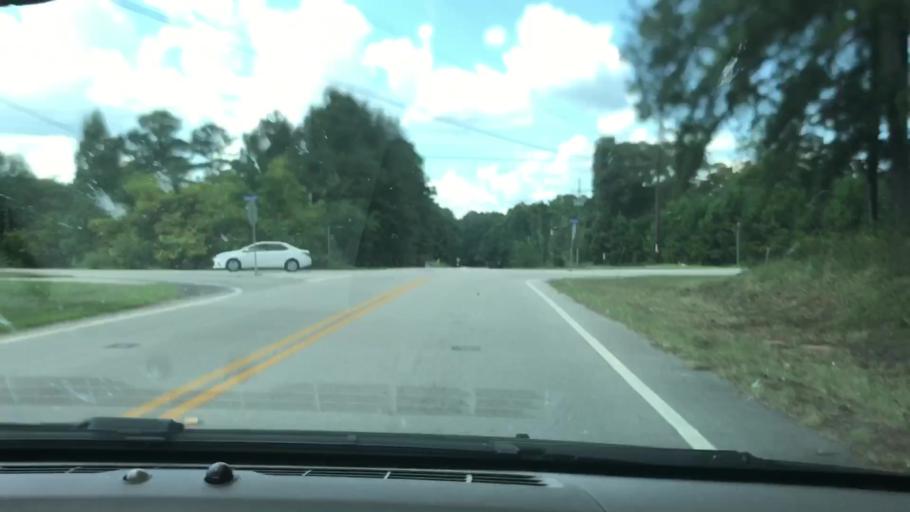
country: US
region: Georgia
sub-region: Troup County
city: La Grange
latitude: 33.1057
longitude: -85.0749
